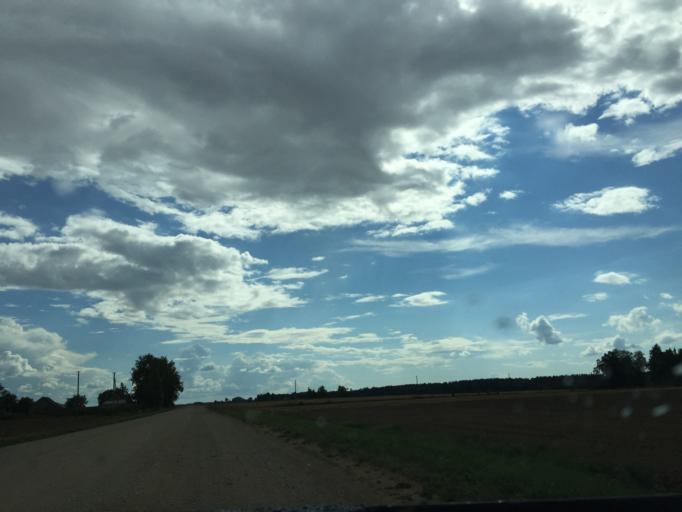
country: LT
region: Siauliu apskritis
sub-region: Joniskis
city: Joniskis
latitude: 56.3283
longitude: 23.5590
